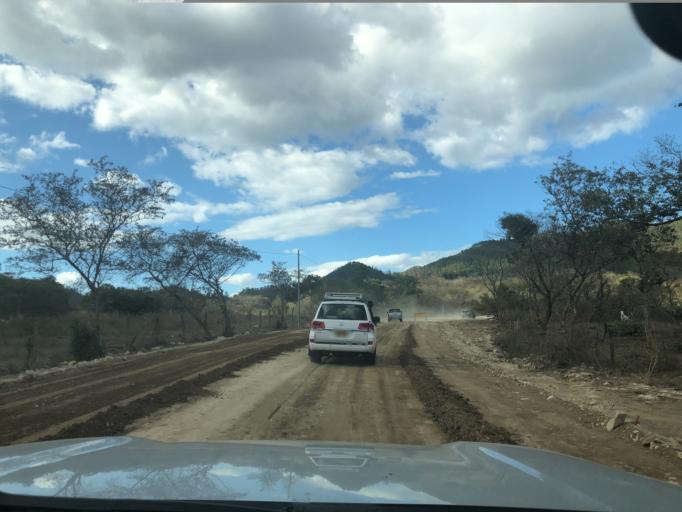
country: NI
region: Nueva Segovia
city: Ocotal
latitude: 13.6633
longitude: -86.6136
